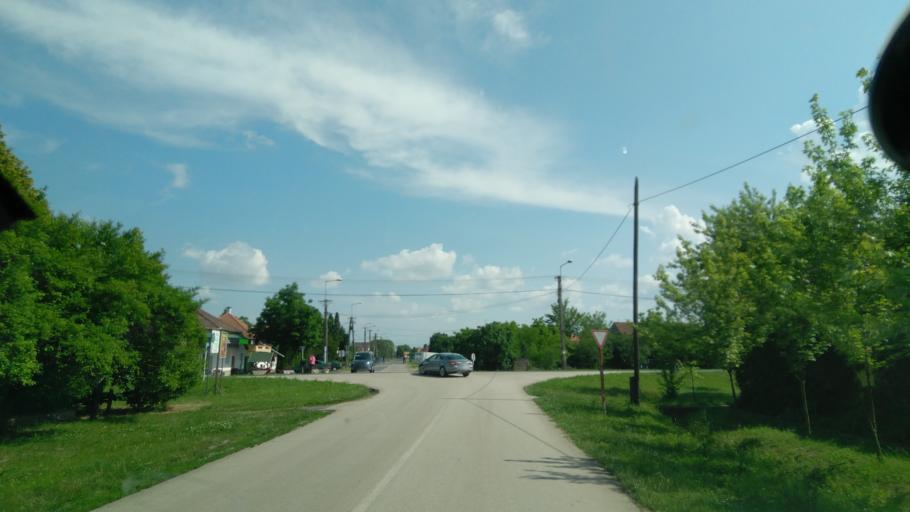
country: HU
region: Bekes
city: Doboz
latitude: 46.7337
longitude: 21.2382
